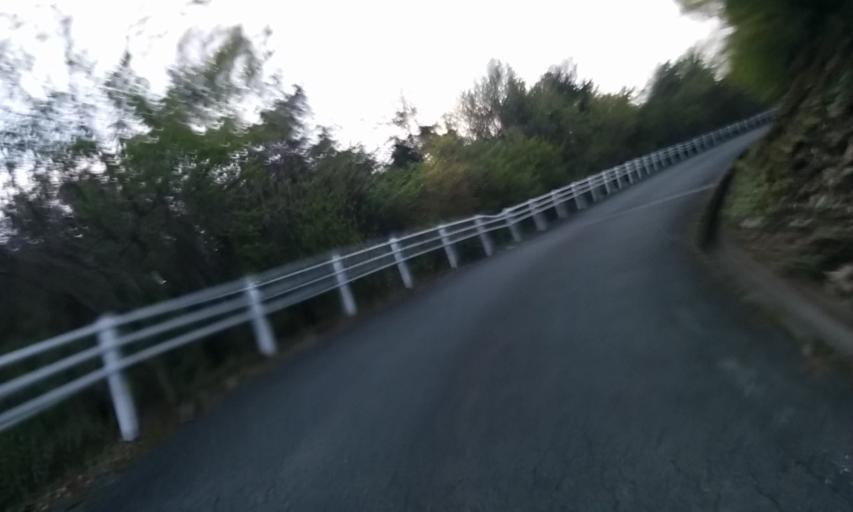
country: JP
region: Ehime
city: Saijo
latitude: 33.7940
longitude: 133.2762
